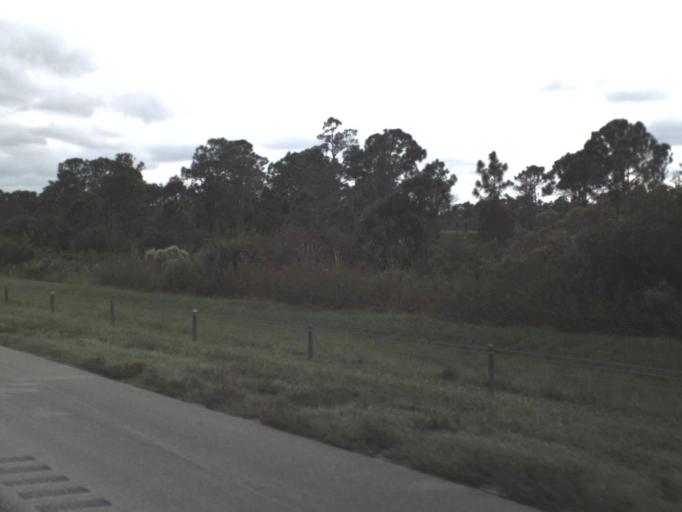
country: US
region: Florida
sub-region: Palm Beach County
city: Limestone Creek
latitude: 26.9703
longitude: -80.1772
